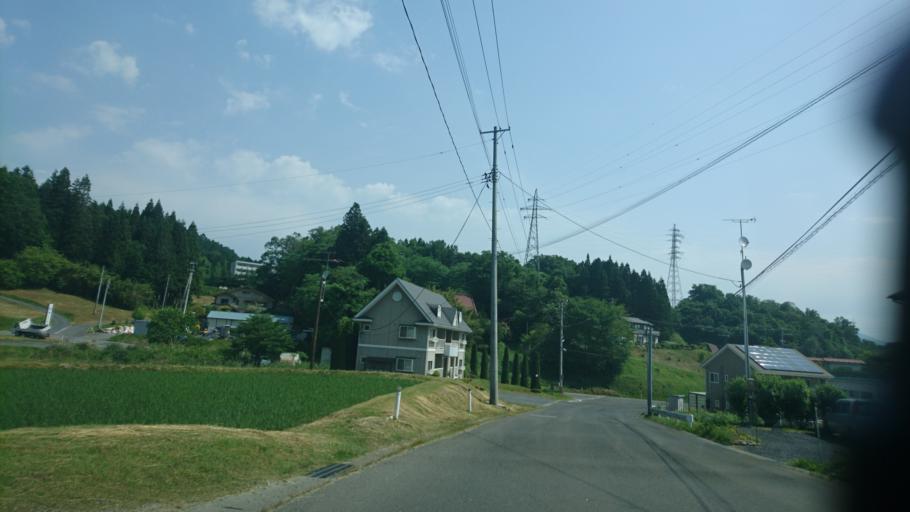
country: JP
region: Iwate
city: Ichinoseki
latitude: 38.9076
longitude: 141.3234
